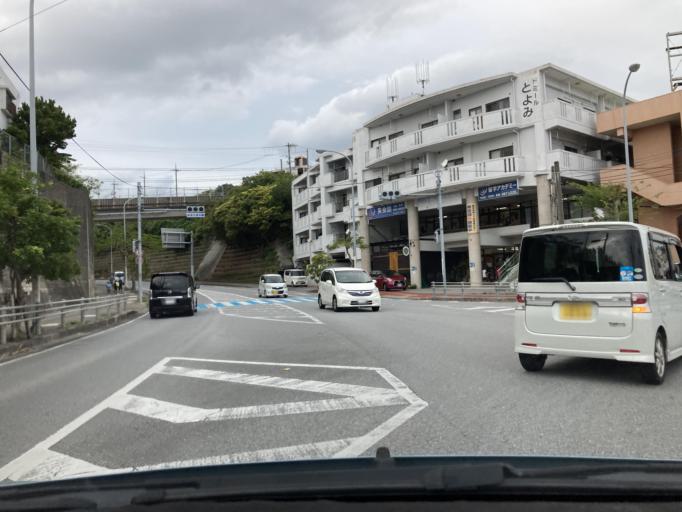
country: JP
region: Okinawa
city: Tomigusuku
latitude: 26.1817
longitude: 127.6810
